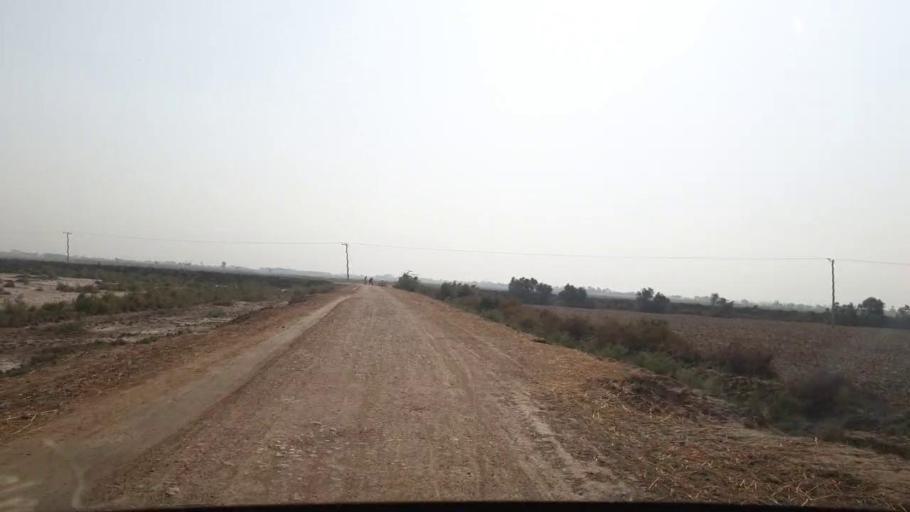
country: PK
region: Sindh
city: Chuhar Jamali
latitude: 24.3723
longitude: 67.9448
